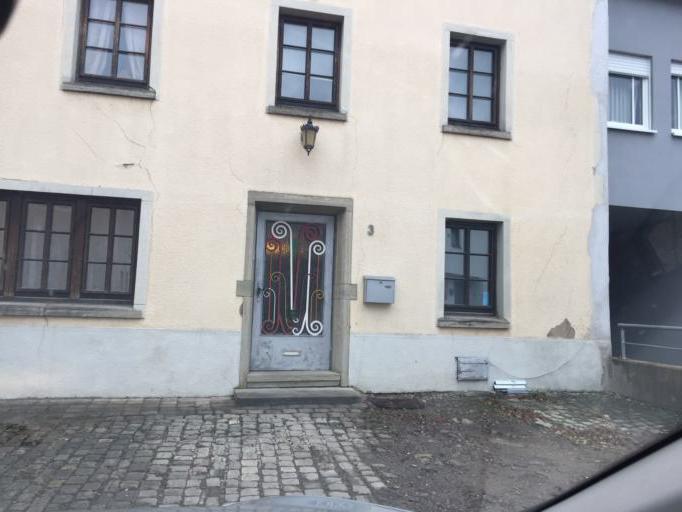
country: LU
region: Diekirch
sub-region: Canton de Diekirch
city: Diekirch
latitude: 49.8655
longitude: 6.1805
